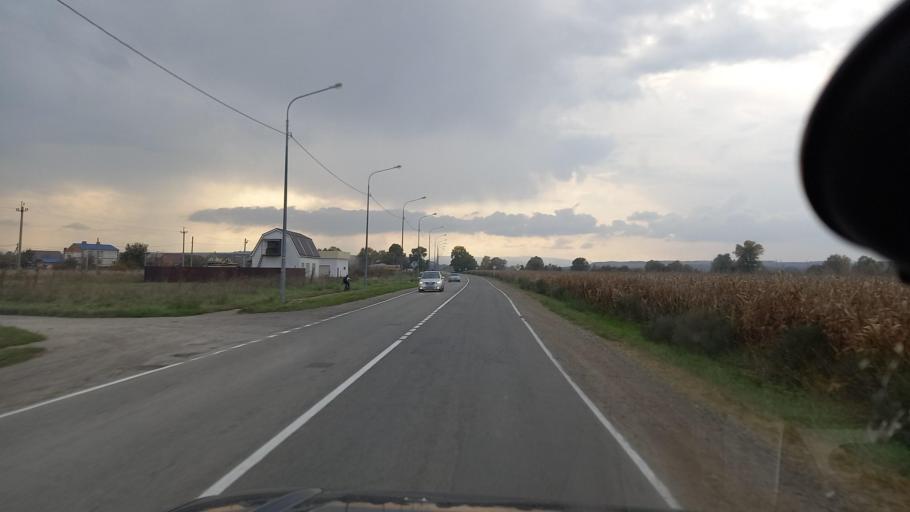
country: RU
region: Krasnodarskiy
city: Mostovskoy
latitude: 44.3990
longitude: 40.7758
